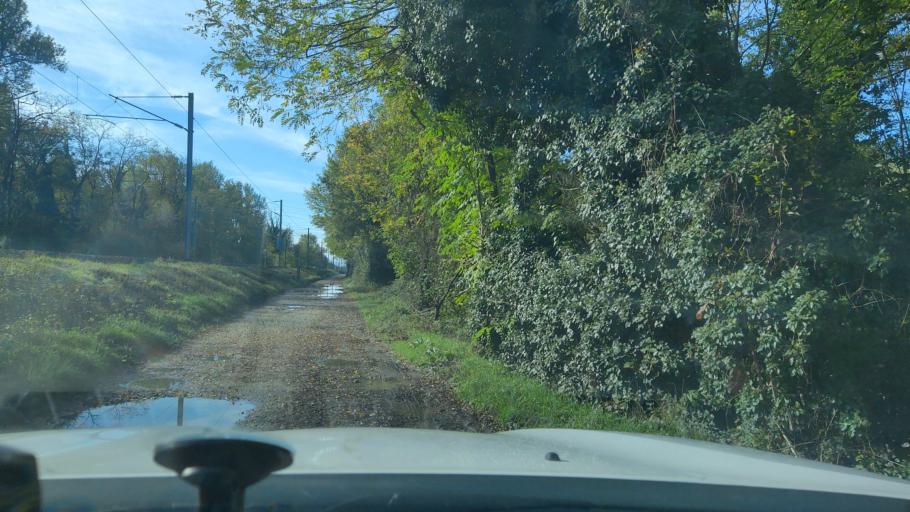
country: FR
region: Rhone-Alpes
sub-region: Departement de la Savoie
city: Montmelian
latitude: 45.4724
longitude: 6.0363
